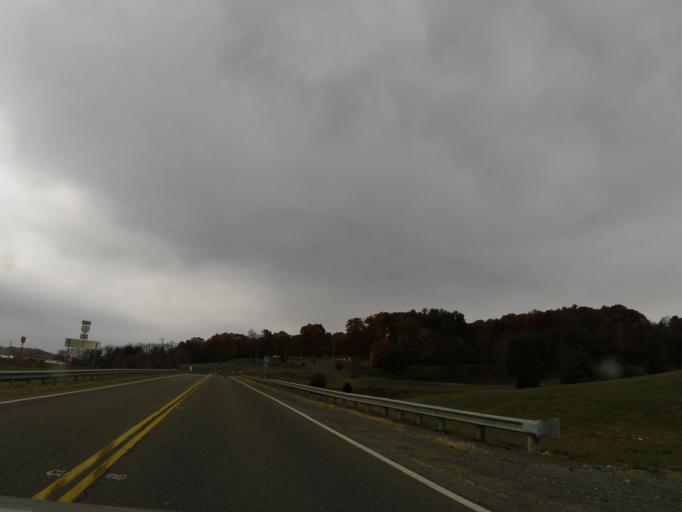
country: US
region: Virginia
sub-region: Bland County
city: Bland
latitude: 37.1012
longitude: -81.1274
